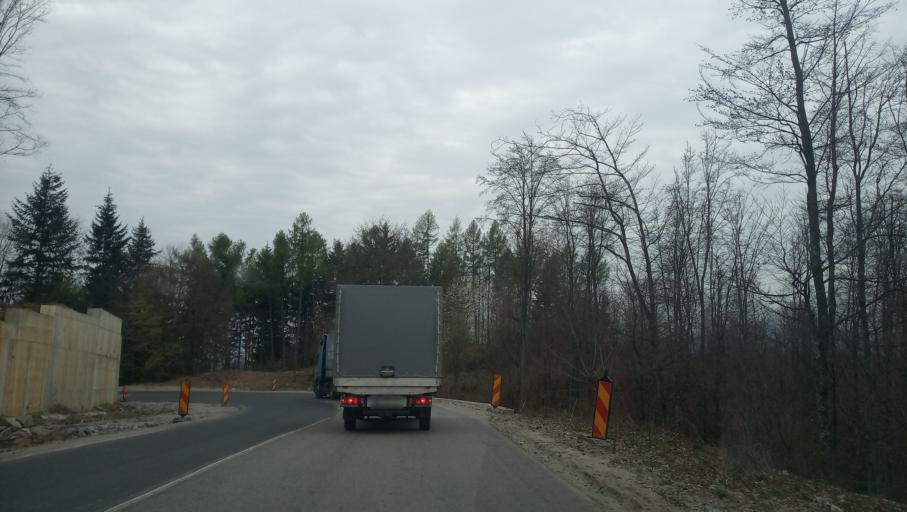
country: RO
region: Bihor
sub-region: Comuna Cristioru de Jos
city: Cristioru de Jos
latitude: 46.3863
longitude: 22.5548
